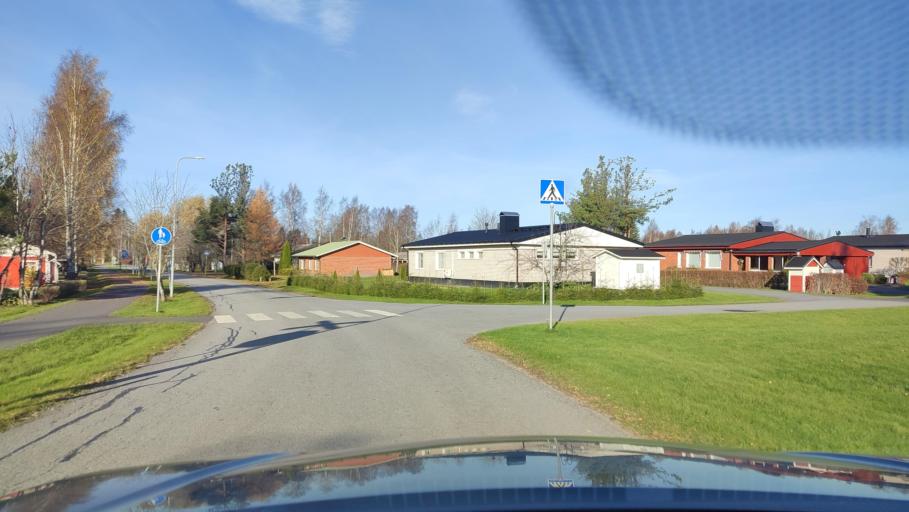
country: FI
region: Southern Ostrobothnia
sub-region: Suupohja
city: Teuva
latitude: 62.4770
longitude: 21.7512
